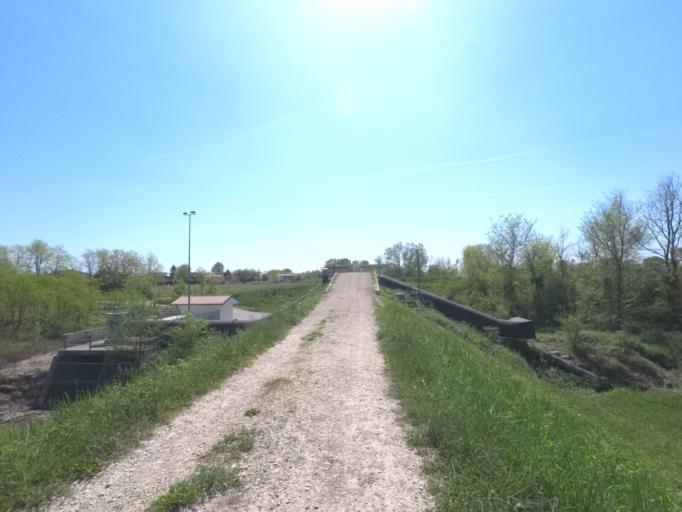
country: IT
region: Friuli Venezia Giulia
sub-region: Provincia di Pordenone
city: Puia-Villanova
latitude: 45.8400
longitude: 12.5594
